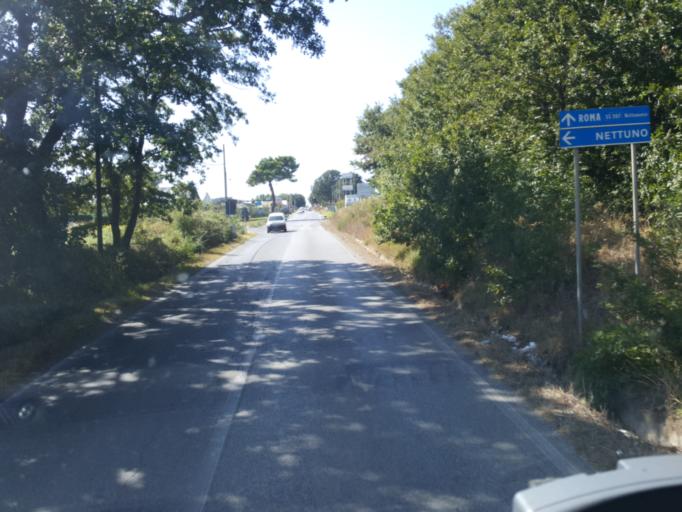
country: IT
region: Latium
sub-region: Citta metropolitana di Roma Capitale
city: Anzio
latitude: 41.5129
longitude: 12.6412
